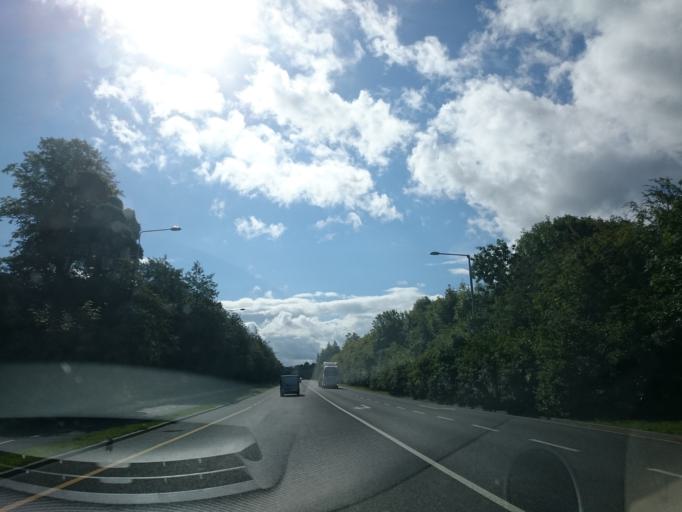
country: IE
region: Leinster
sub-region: Kilkenny
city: Kilkenny
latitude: 52.6421
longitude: -7.2622
